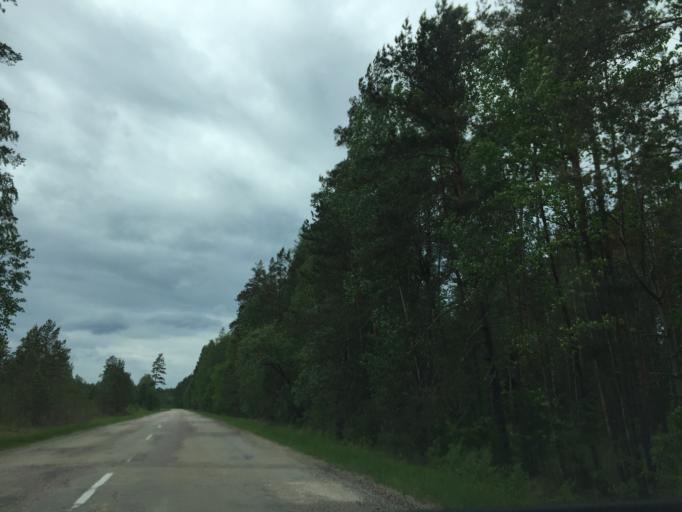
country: LV
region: Aglona
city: Aglona
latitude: 56.1448
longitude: 27.2033
